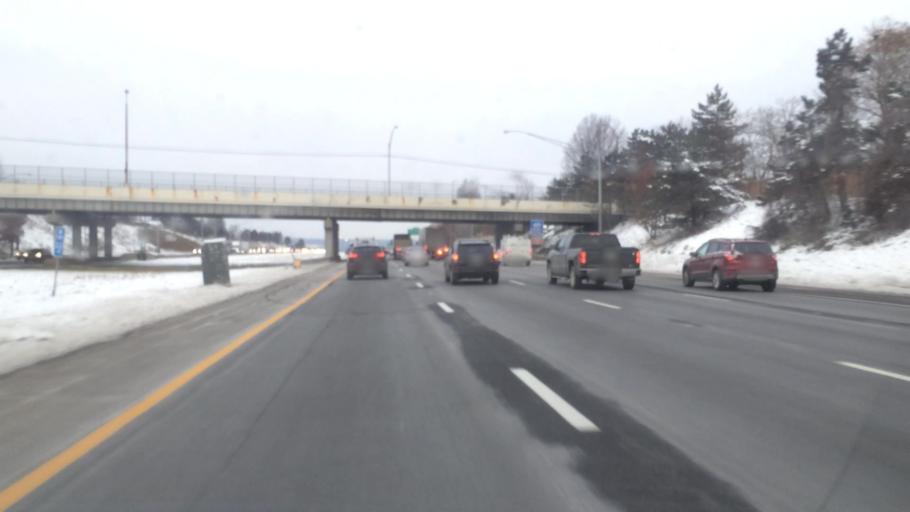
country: US
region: Ohio
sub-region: Cuyahoga County
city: Garfield Heights
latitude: 41.4141
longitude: -81.6025
